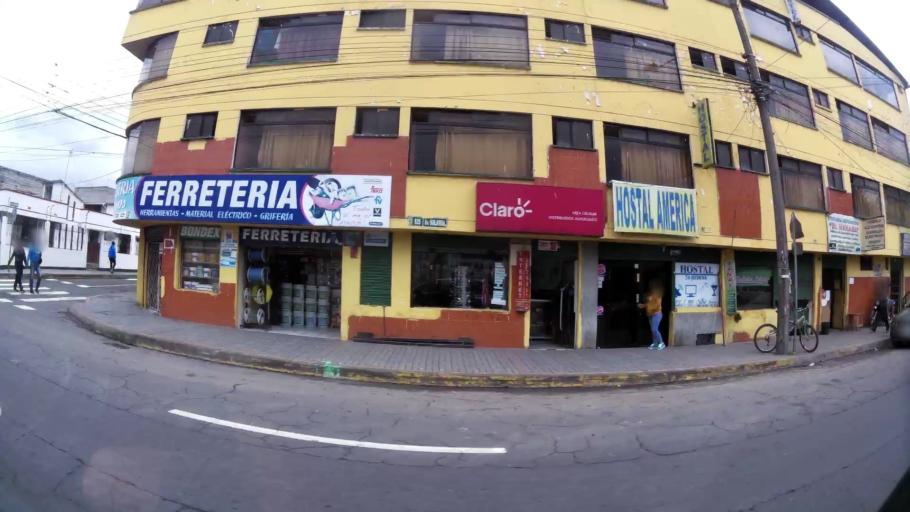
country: EC
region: Pichincha
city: Quito
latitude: -0.2745
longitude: -78.5409
